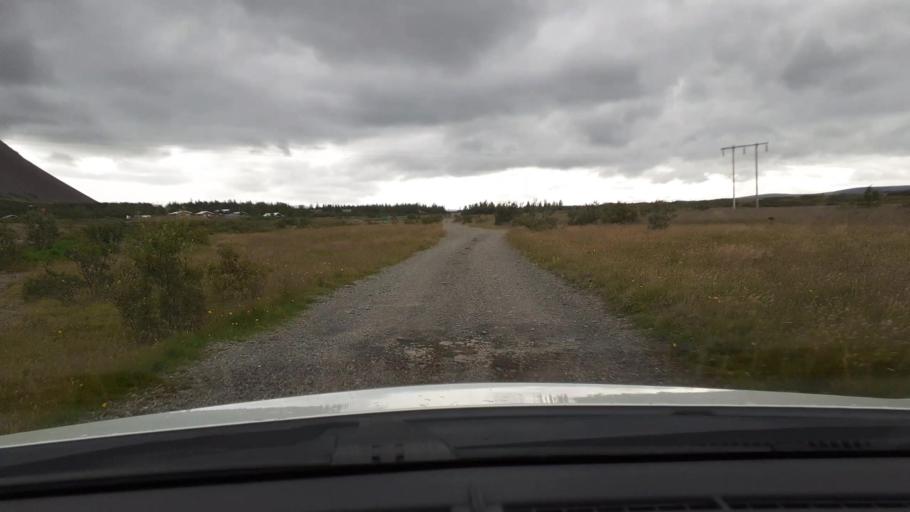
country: IS
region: West
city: Borgarnes
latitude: 64.4625
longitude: -21.9581
